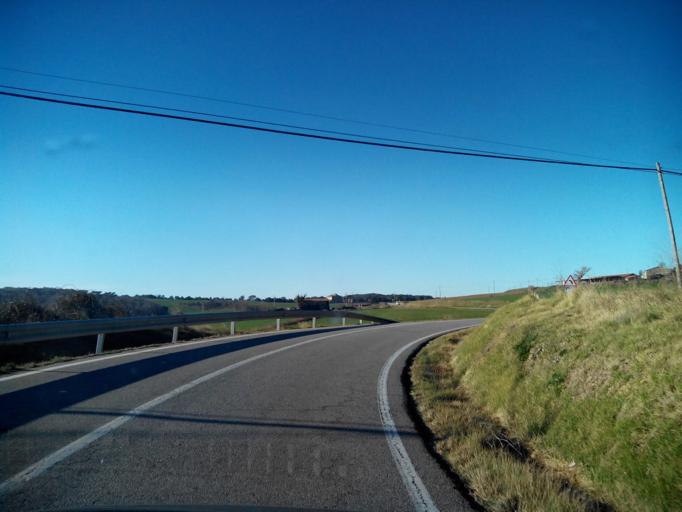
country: ES
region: Catalonia
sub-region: Provincia de Barcelona
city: Avia
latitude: 42.0757
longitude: 1.8129
